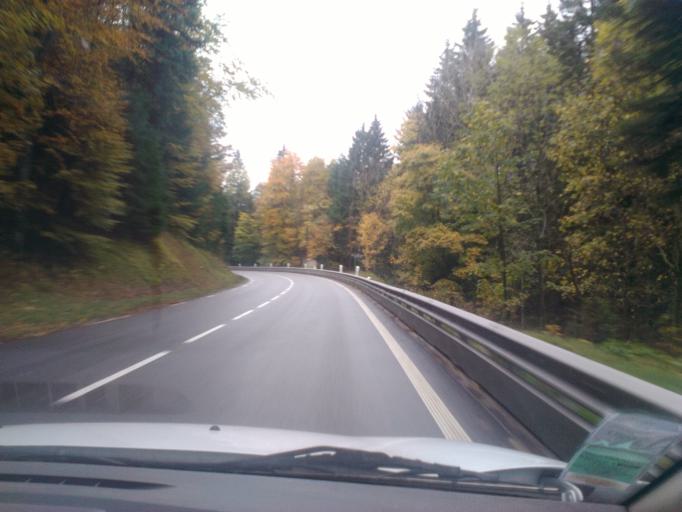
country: FR
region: Lorraine
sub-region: Departement des Vosges
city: Xonrupt-Longemer
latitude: 48.1039
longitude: 6.9062
